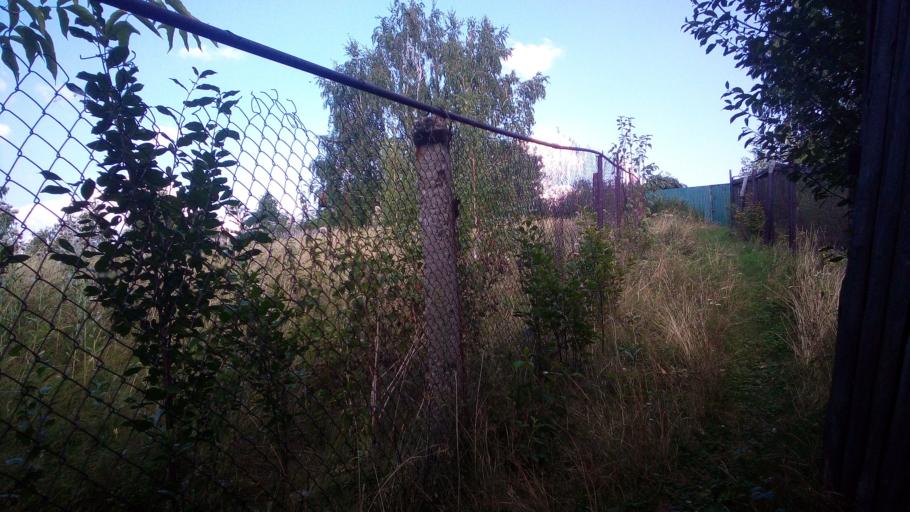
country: RU
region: Chelyabinsk
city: Ozersk
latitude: 55.7867
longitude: 60.7443
